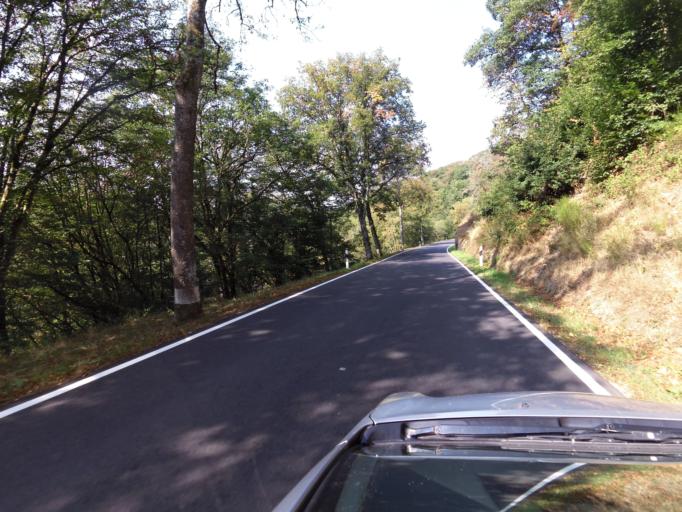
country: LU
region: Diekirch
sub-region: Canton de Wiltz
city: Goesdorf
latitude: 49.9092
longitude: 5.9721
